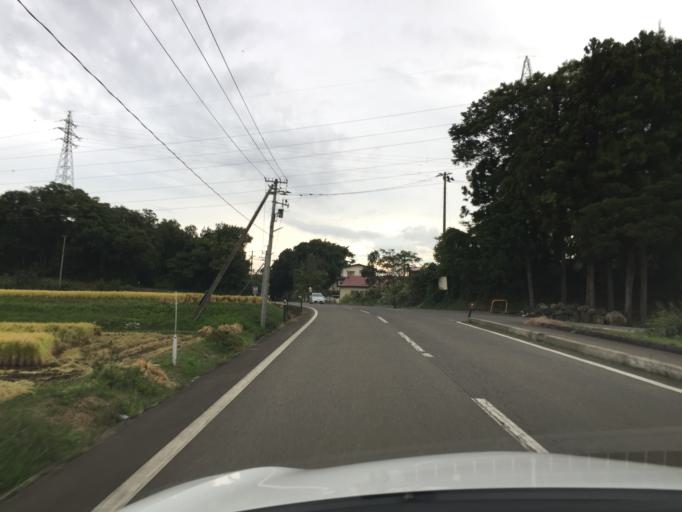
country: JP
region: Fukushima
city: Kitakata
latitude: 37.5724
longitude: 139.9486
